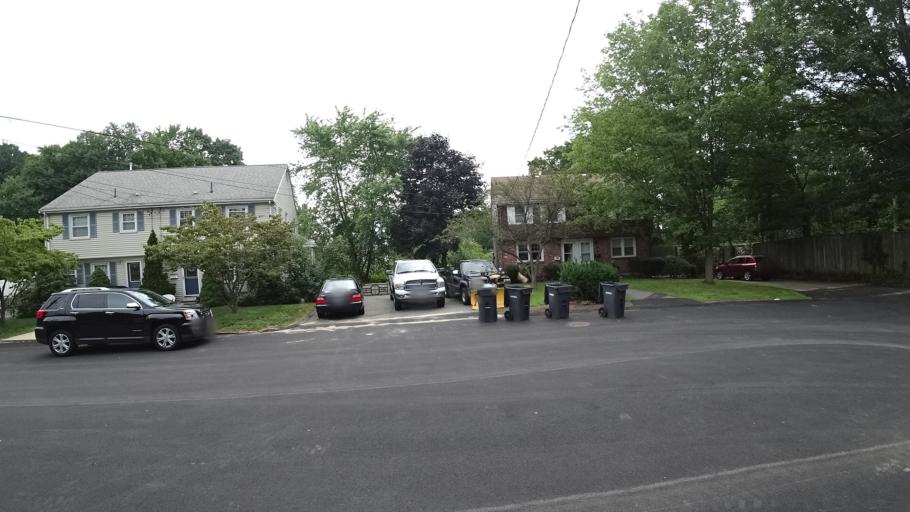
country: US
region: Massachusetts
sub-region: Norfolk County
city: Dedham
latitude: 42.2360
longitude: -71.1456
